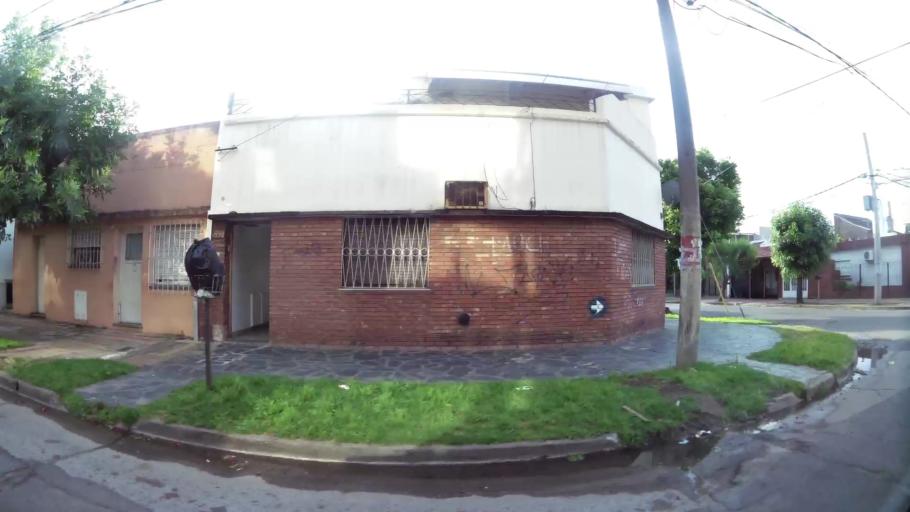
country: AR
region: Buenos Aires
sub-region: Partido de Moron
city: Moron
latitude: -34.6584
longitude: -58.6215
